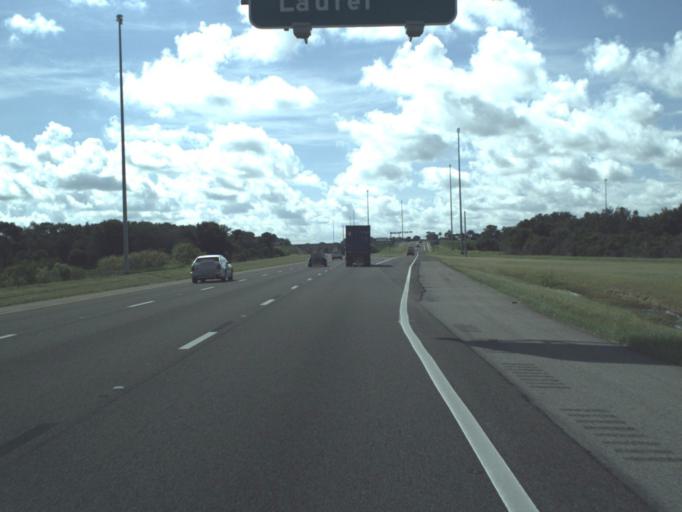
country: US
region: Florida
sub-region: Sarasota County
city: Nokomis
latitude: 27.1430
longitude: -82.4147
